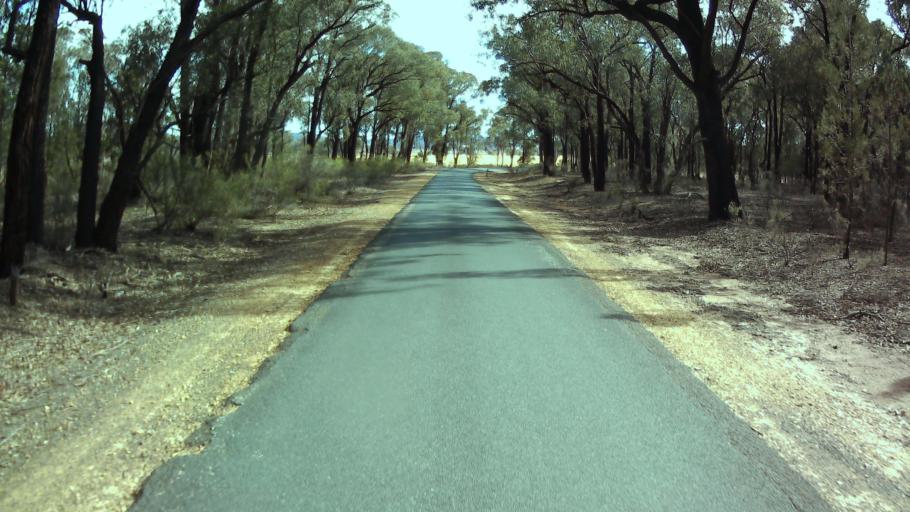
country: AU
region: New South Wales
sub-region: Weddin
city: Grenfell
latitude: -33.8550
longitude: 148.2175
